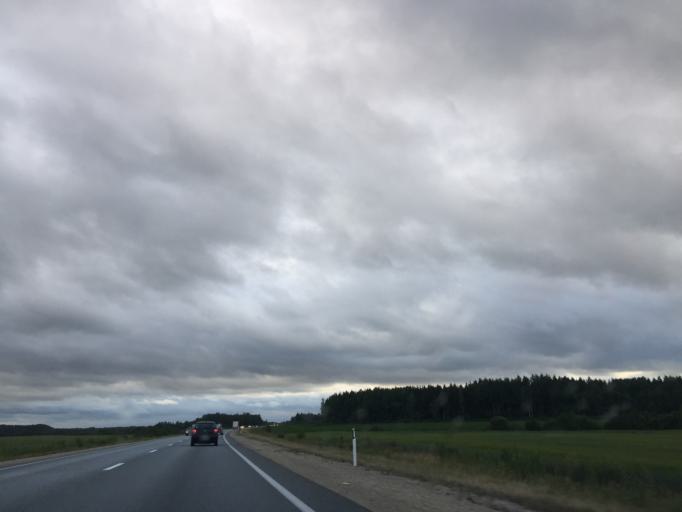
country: LV
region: Koknese
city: Koknese
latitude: 56.6703
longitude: 25.4029
